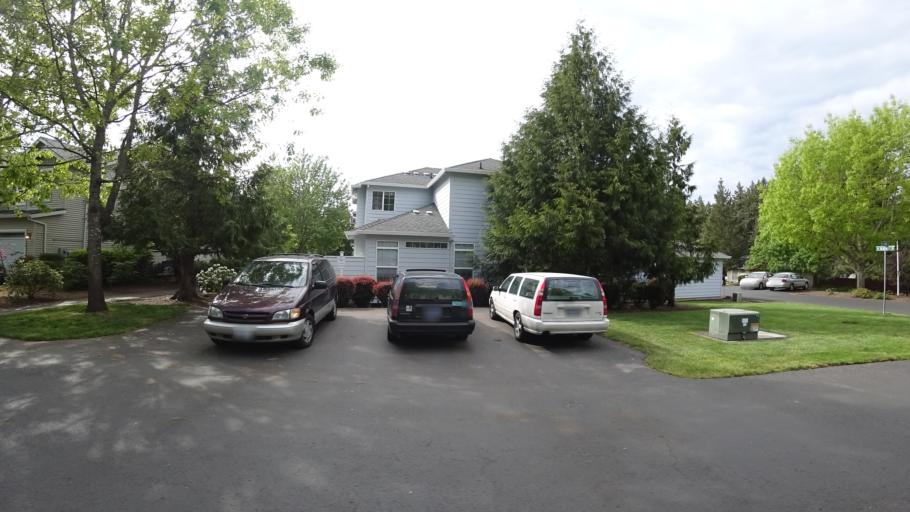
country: US
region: Oregon
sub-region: Washington County
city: Hillsboro
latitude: 45.4961
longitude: -122.9557
